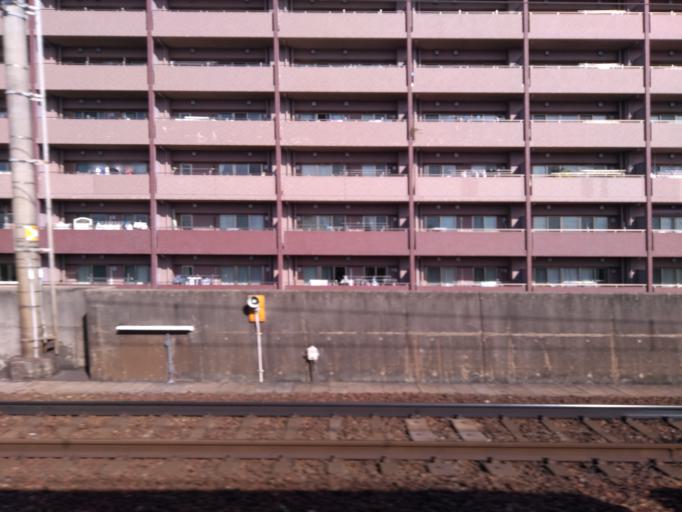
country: JP
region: Osaka
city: Ikeda
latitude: 34.8235
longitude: 135.4226
